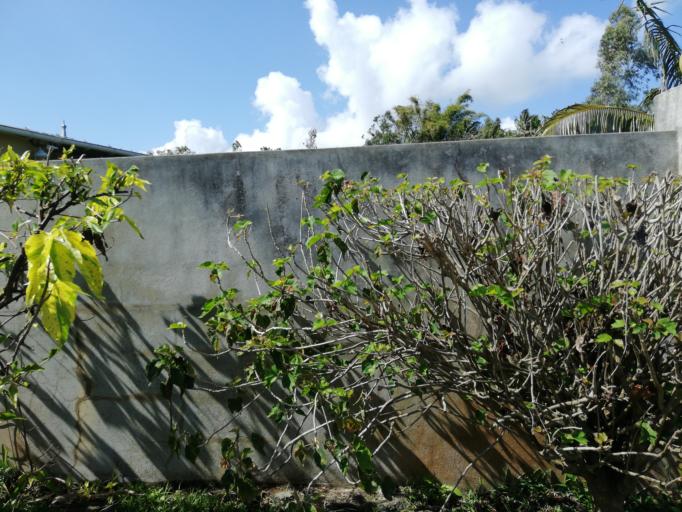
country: MU
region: Moka
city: Moka
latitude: -20.2167
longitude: 57.5023
